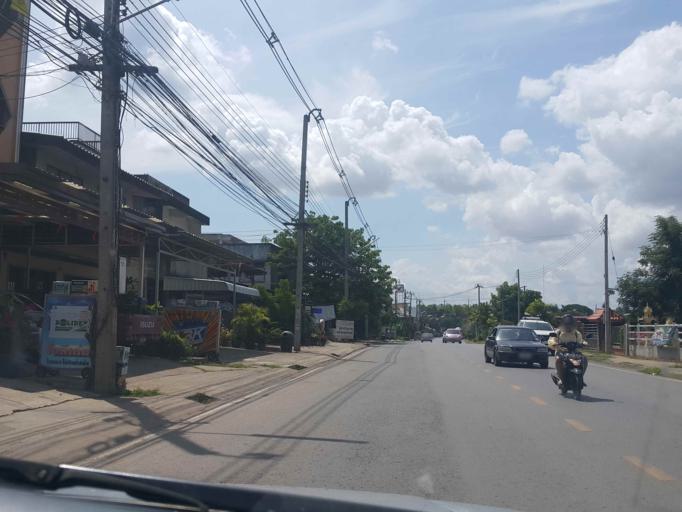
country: TH
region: Phayao
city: Phayao
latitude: 19.1649
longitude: 99.9093
